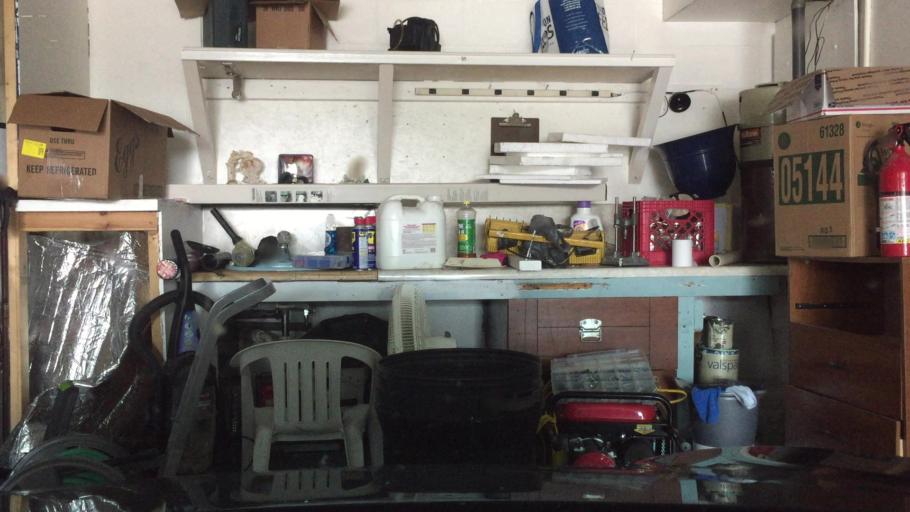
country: US
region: Virginia
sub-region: Pulaski County
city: Pulaski
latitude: 36.9553
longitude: -80.8770
